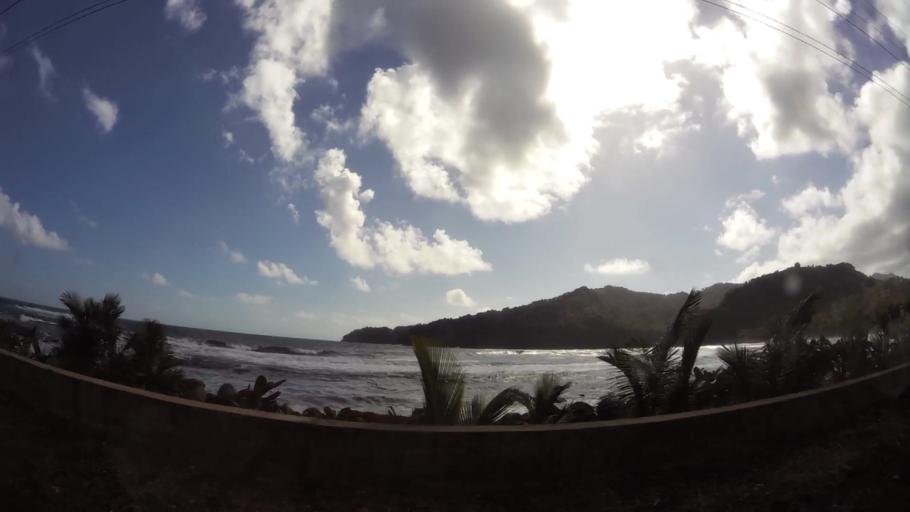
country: DM
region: Saint Andrew
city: Marigot
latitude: 15.5239
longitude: -61.2755
